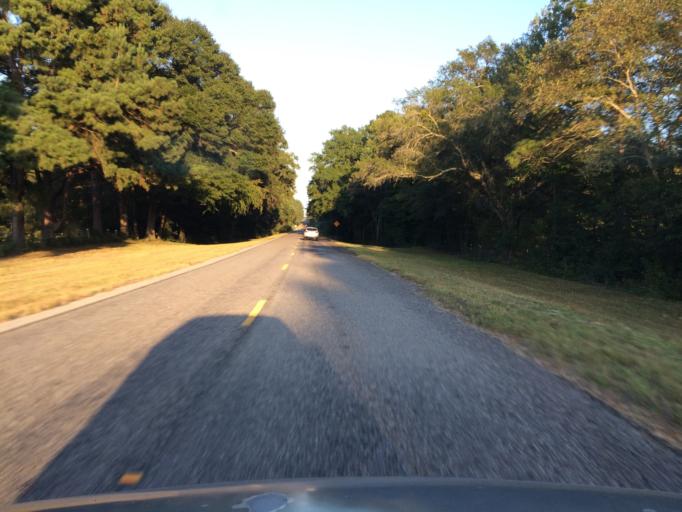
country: US
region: Texas
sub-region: Wood County
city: Hawkins
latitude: 32.7333
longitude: -95.2337
